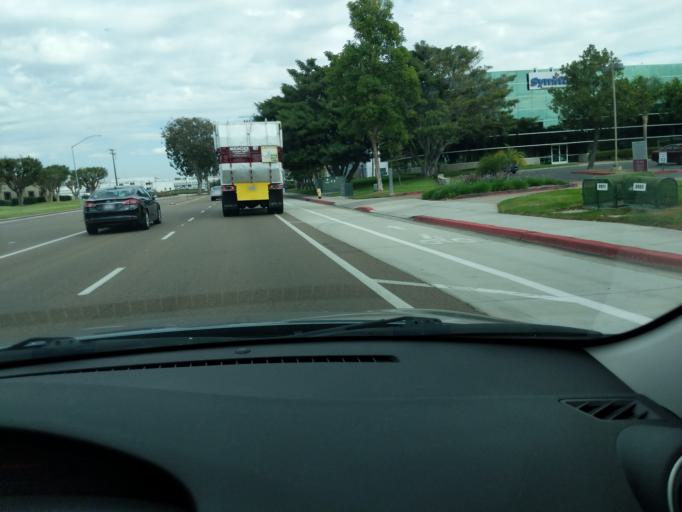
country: US
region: California
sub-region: San Diego County
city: San Diego
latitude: 32.8212
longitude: -117.1359
